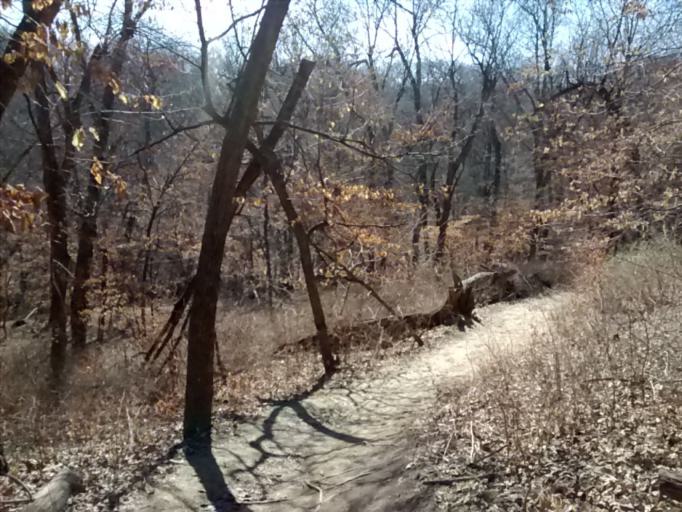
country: US
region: Nebraska
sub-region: Sarpy County
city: Bellevue
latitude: 41.1786
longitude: -95.9143
